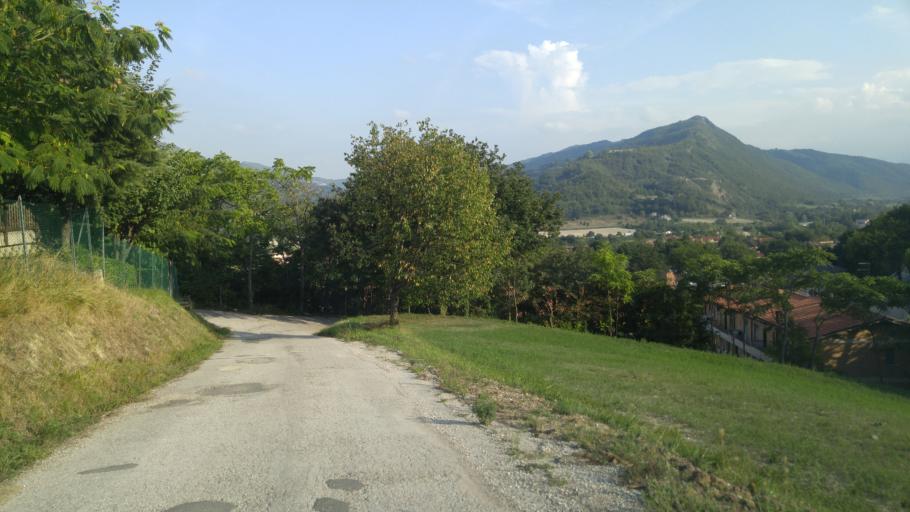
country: IT
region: The Marches
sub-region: Provincia di Pesaro e Urbino
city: Acqualagna
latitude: 43.6265
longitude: 12.6713
